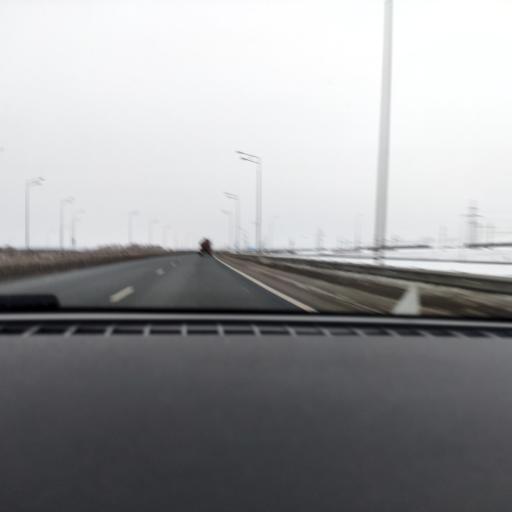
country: RU
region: Samara
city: Smyshlyayevka
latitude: 53.1330
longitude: 50.4253
